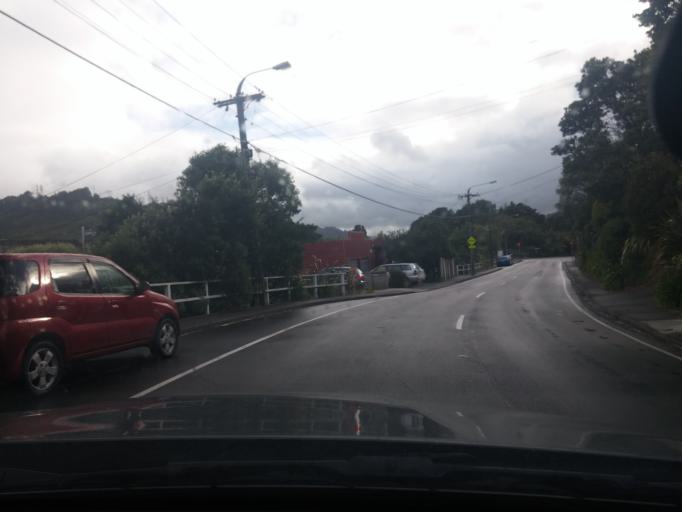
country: NZ
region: Wellington
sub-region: Wellington City
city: Kelburn
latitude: -41.2689
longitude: 174.7554
